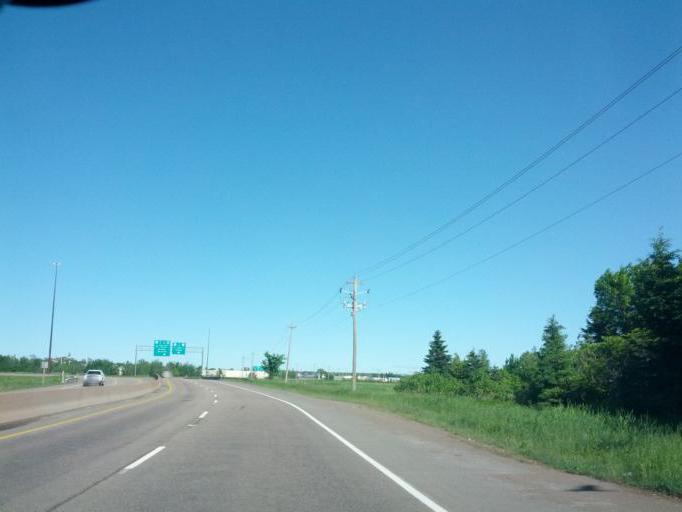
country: CA
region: New Brunswick
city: Moncton
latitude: 46.0973
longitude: -64.7738
